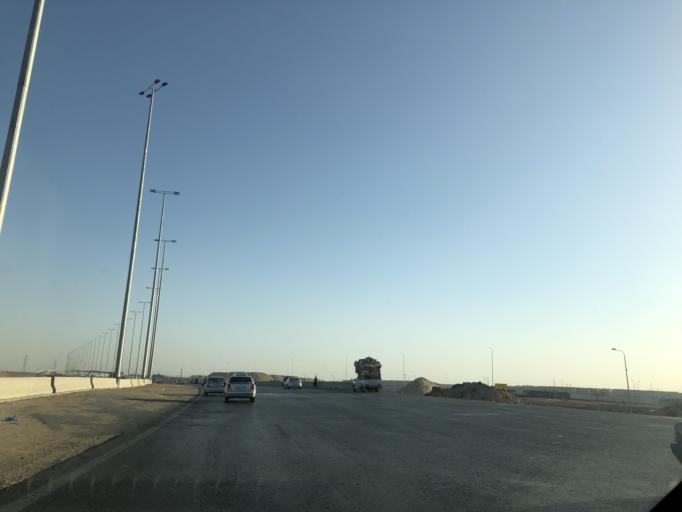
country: EG
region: Al Jizah
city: Al Jizah
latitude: 29.9406
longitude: 31.0981
